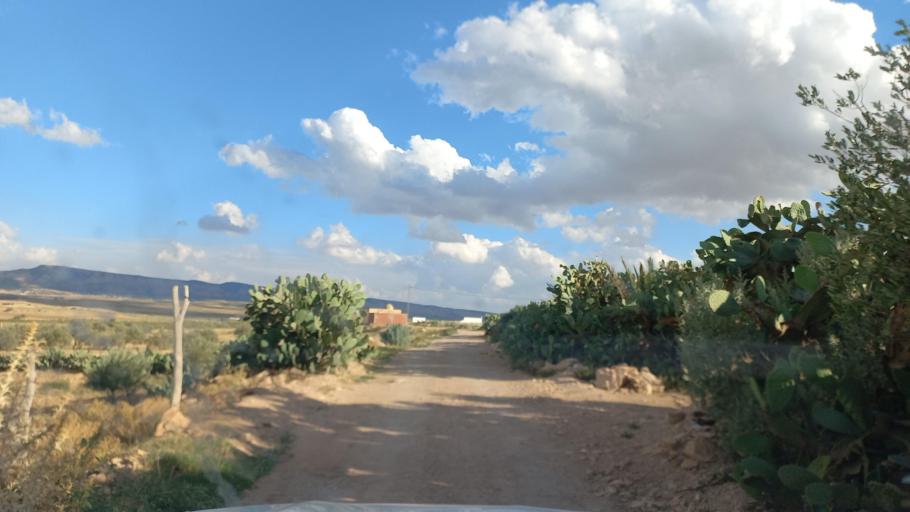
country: TN
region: Al Qasrayn
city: Sbiba
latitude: 35.3812
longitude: 9.0727
